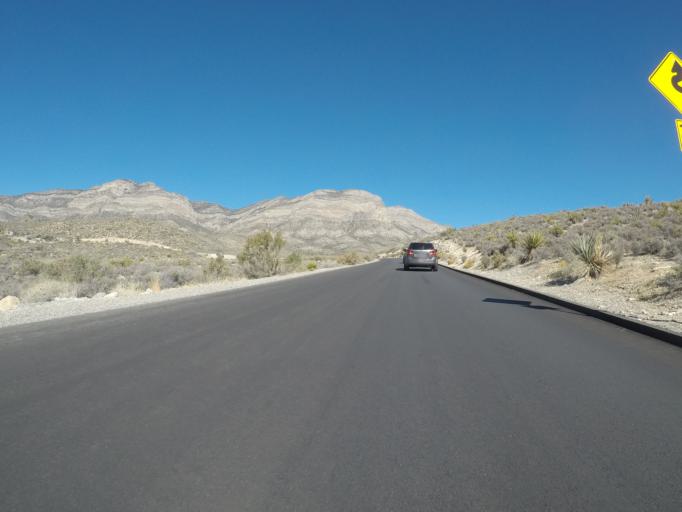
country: US
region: Nevada
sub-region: Clark County
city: Summerlin South
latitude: 36.1707
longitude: -115.4627
